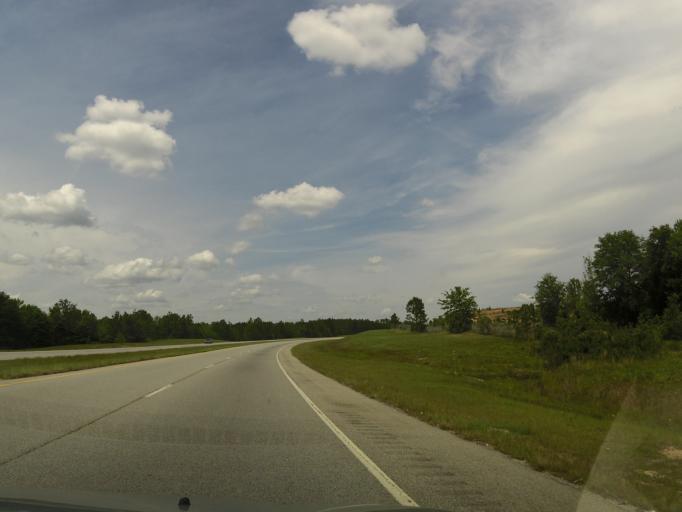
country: US
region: Georgia
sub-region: Emanuel County
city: Swainsboro
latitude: 32.6135
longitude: -82.3808
